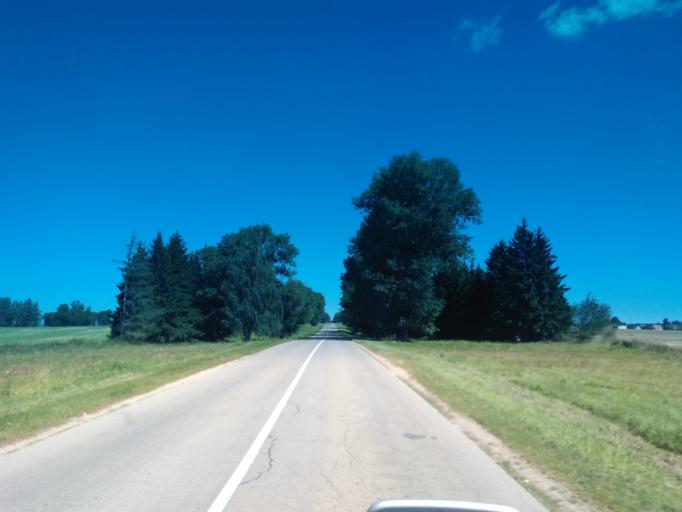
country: BY
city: Fanipol
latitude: 53.6788
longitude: 27.3586
